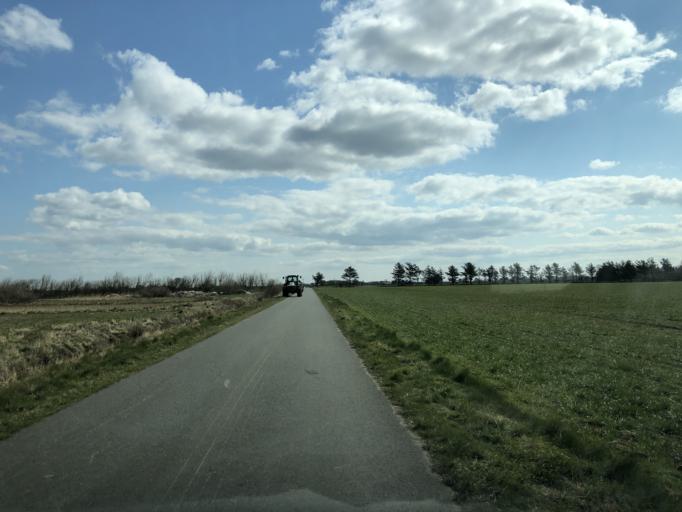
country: DK
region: Central Jutland
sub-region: Holstebro Kommune
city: Ulfborg
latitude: 56.4017
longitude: 8.1961
